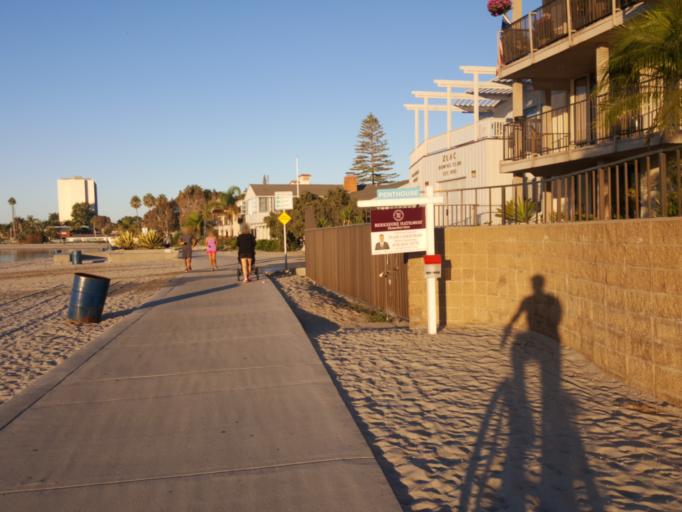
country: US
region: California
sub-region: San Diego County
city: La Jolla
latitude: 32.7917
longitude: -117.2472
